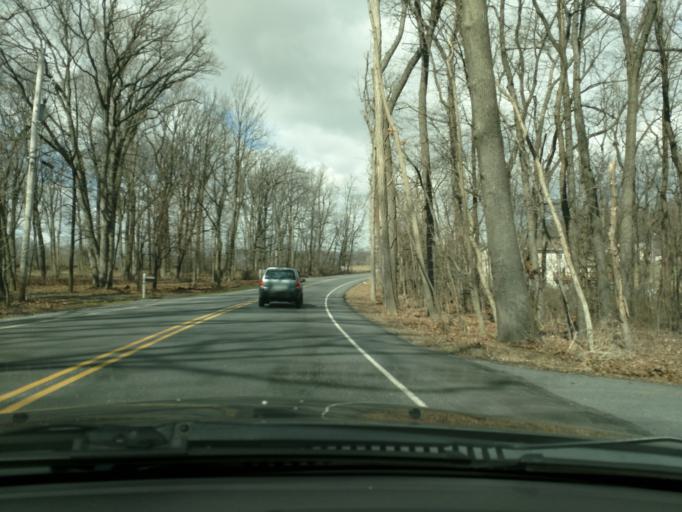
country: US
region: Pennsylvania
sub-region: Lebanon County
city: Myerstown
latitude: 40.4018
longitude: -76.3043
